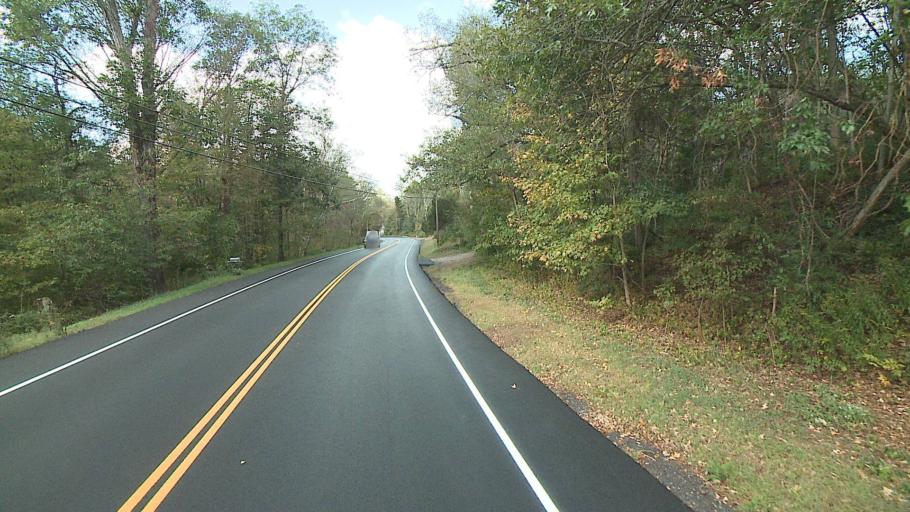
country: US
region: Connecticut
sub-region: New Haven County
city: Prospect
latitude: 41.4567
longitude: -72.9800
